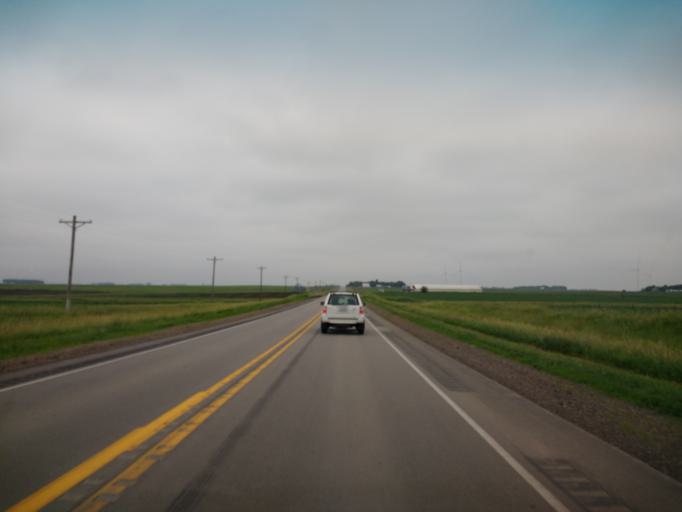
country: US
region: Iowa
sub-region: O'Brien County
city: Hartley
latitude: 43.1850
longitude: -95.5100
